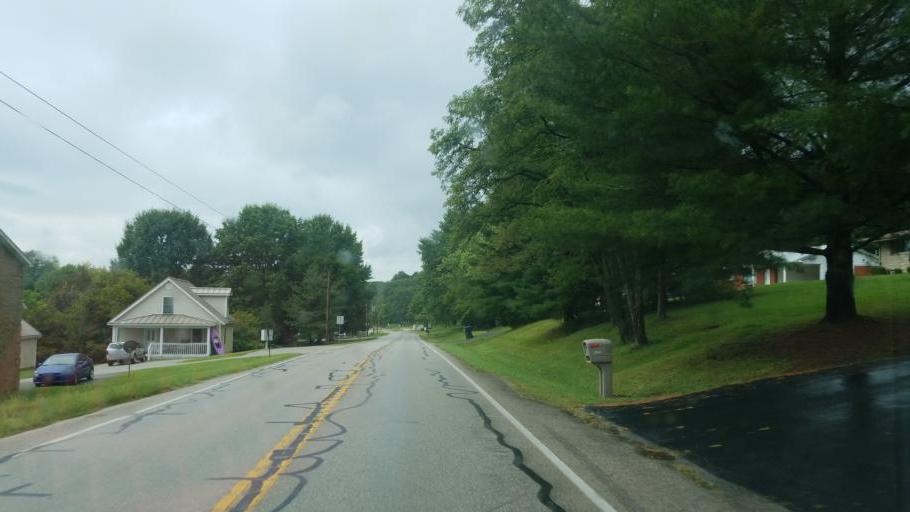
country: US
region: Kentucky
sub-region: Rowan County
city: Morehead
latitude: 38.1567
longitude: -83.4639
